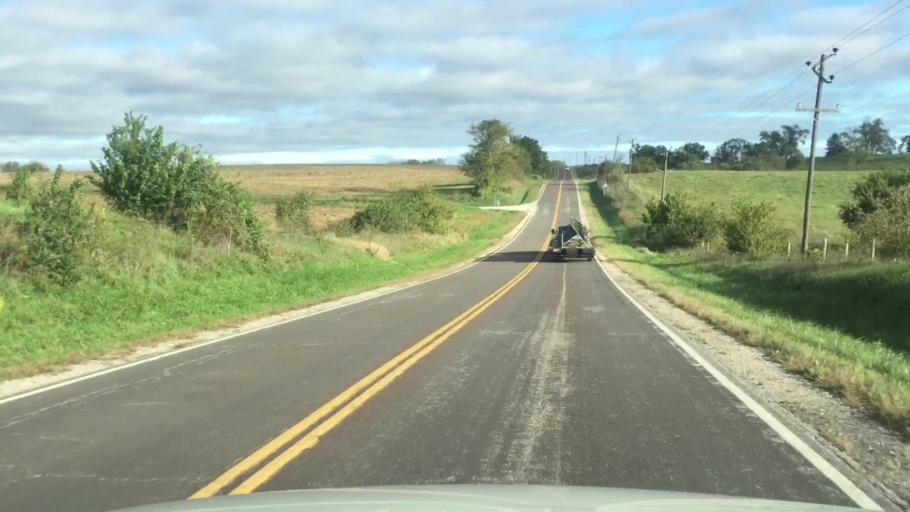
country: US
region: Missouri
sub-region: Howard County
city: New Franklin
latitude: 39.0777
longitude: -92.7456
